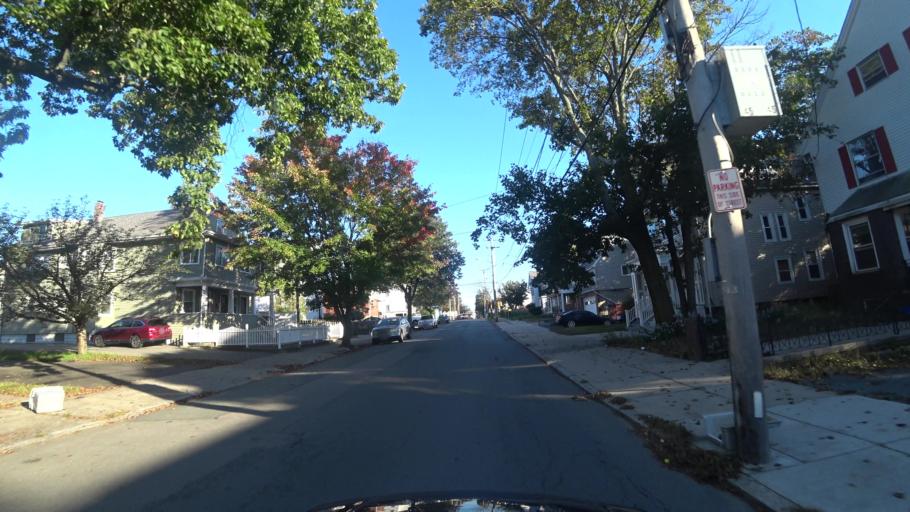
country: US
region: Massachusetts
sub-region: Middlesex County
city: Malden
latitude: 42.4170
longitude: -71.0608
